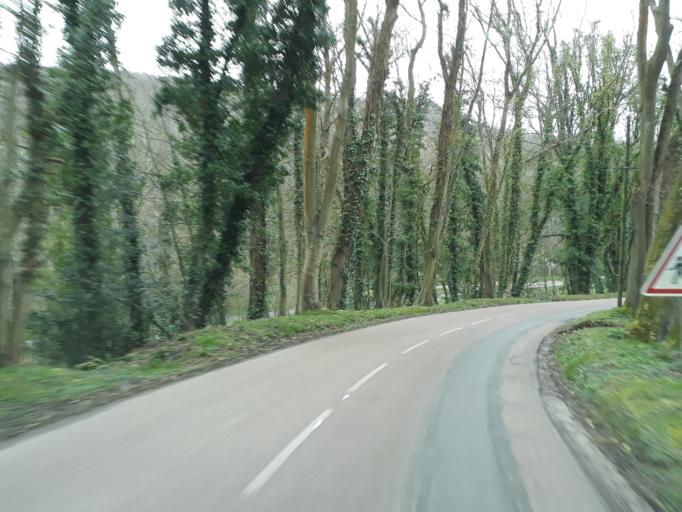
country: FR
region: Haute-Normandie
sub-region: Departement de la Seine-Maritime
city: Yport
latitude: 49.7330
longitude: 0.2906
